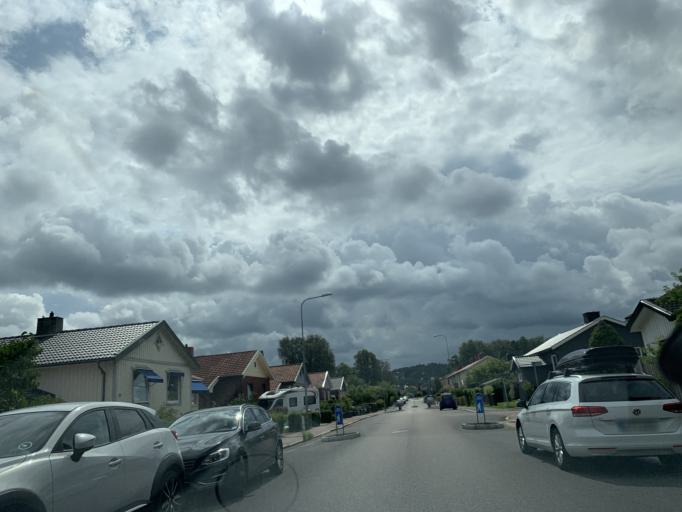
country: SE
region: Vaestra Goetaland
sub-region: Goteborg
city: Eriksbo
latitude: 57.7398
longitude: 12.0584
